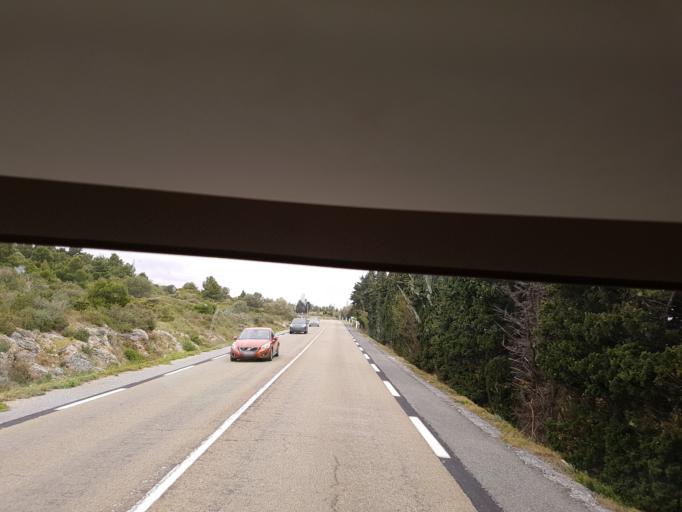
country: FR
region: Languedoc-Roussillon
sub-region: Departement de l'Aude
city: Leucate
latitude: 42.8851
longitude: 2.9939
